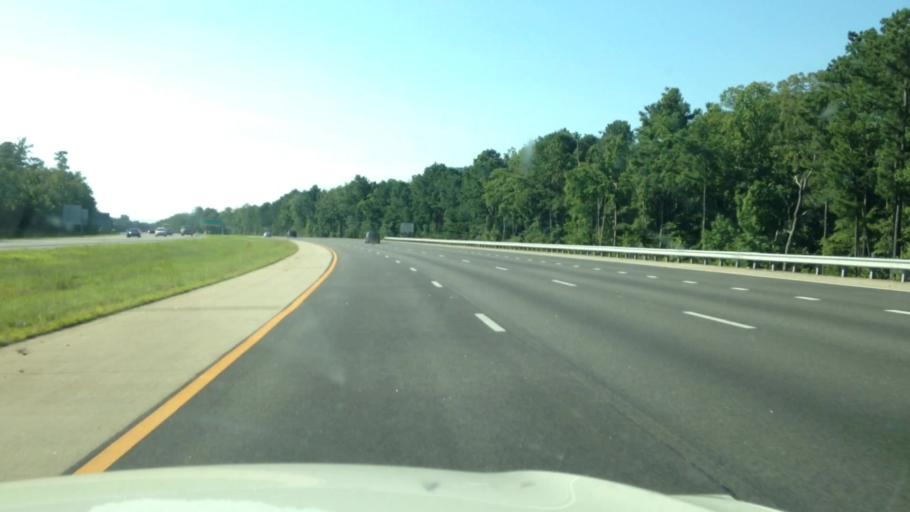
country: US
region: Virginia
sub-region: Chesterfield County
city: Enon
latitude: 37.3518
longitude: -77.3346
